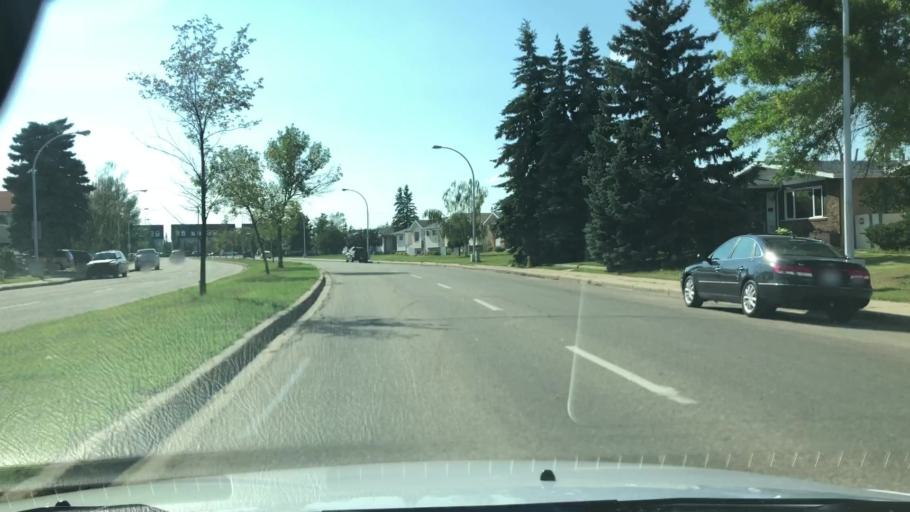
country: CA
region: Alberta
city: Edmonton
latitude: 53.6067
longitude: -113.4878
